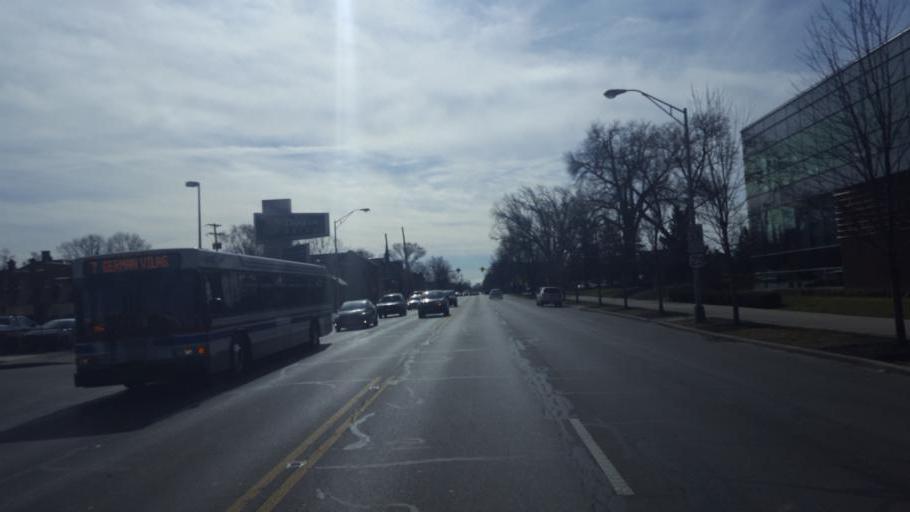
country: US
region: Ohio
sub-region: Franklin County
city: Columbus
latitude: 39.9487
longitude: -82.9981
